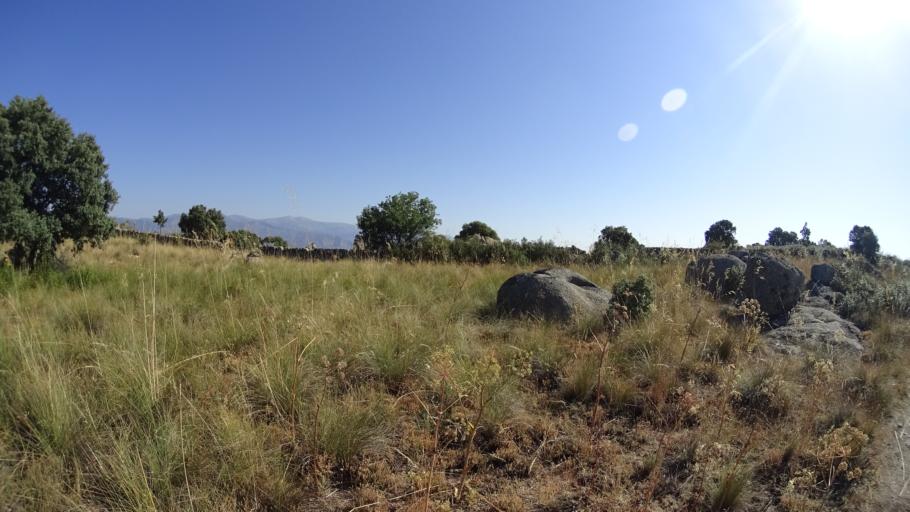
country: ES
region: Madrid
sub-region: Provincia de Madrid
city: Moralzarzal
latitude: 40.6504
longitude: -3.9439
